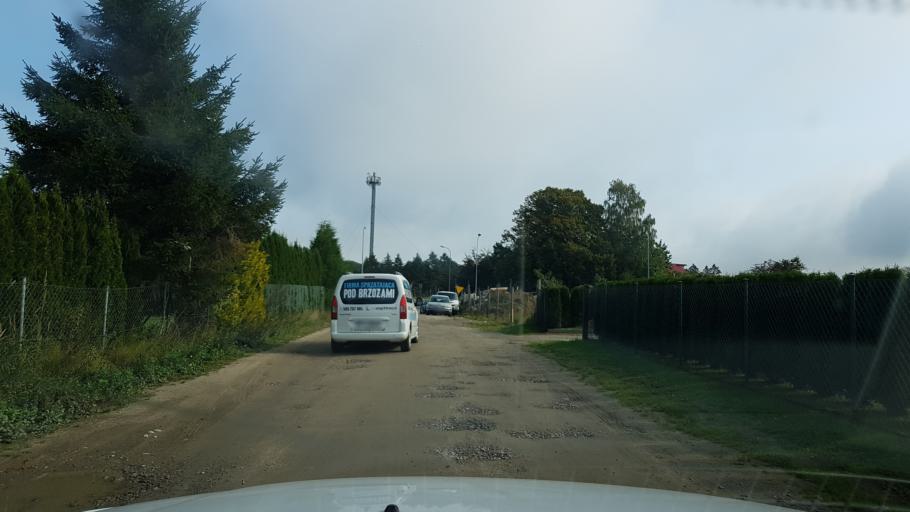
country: PL
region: West Pomeranian Voivodeship
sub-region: Powiat kolobrzeski
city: Ustronie Morskie
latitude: 54.2134
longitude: 15.7627
